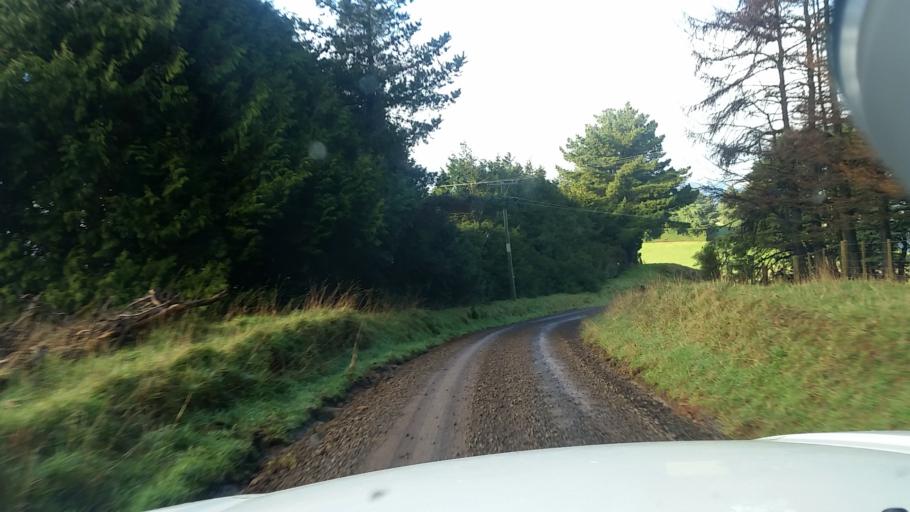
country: NZ
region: Canterbury
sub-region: Christchurch City
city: Christchurch
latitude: -43.7458
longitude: 172.9080
